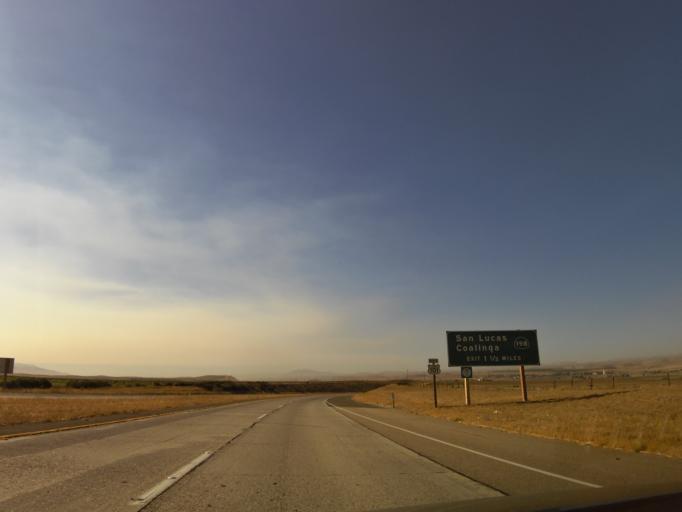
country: US
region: California
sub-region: Monterey County
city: King City
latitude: 36.0972
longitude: -121.0247
